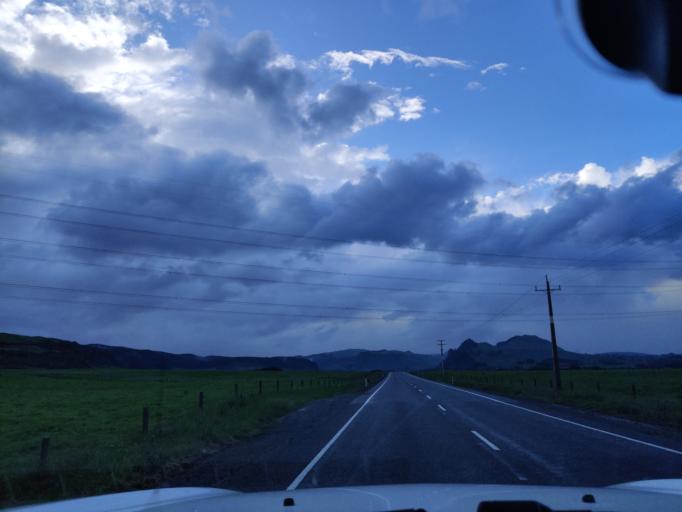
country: NZ
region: Waikato
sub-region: South Waikato District
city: Tokoroa
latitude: -38.3968
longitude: 175.7861
